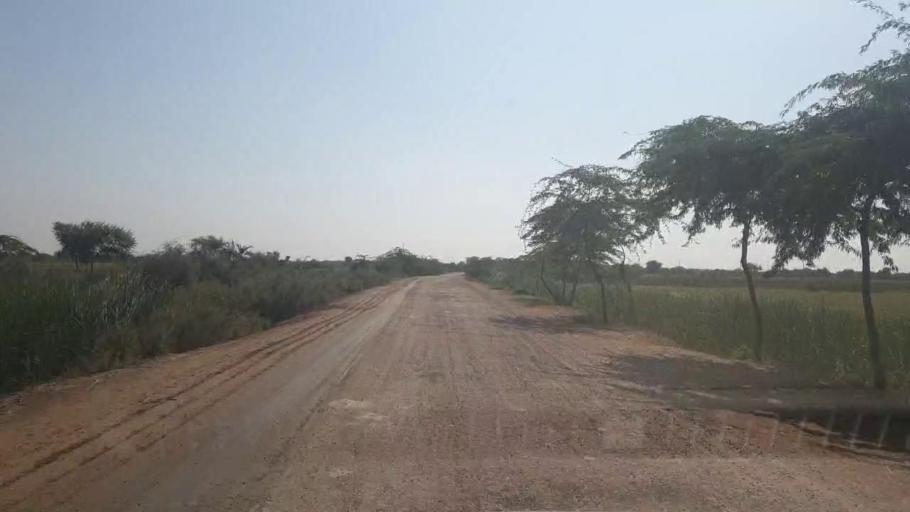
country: PK
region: Sindh
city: Badin
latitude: 24.5877
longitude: 68.8458
